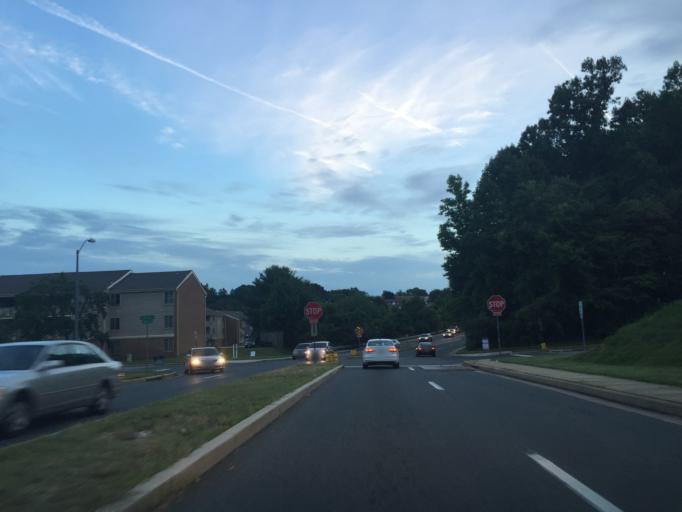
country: US
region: Maryland
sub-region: Baltimore County
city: Carney
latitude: 39.3836
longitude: -76.5101
